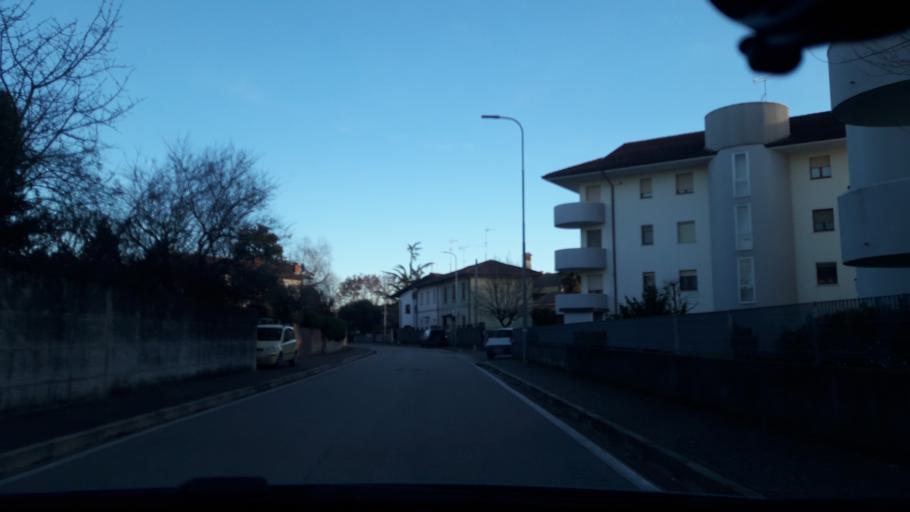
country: IT
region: Friuli Venezia Giulia
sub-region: Provincia di Udine
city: Udine
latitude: 46.0491
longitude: 13.2466
